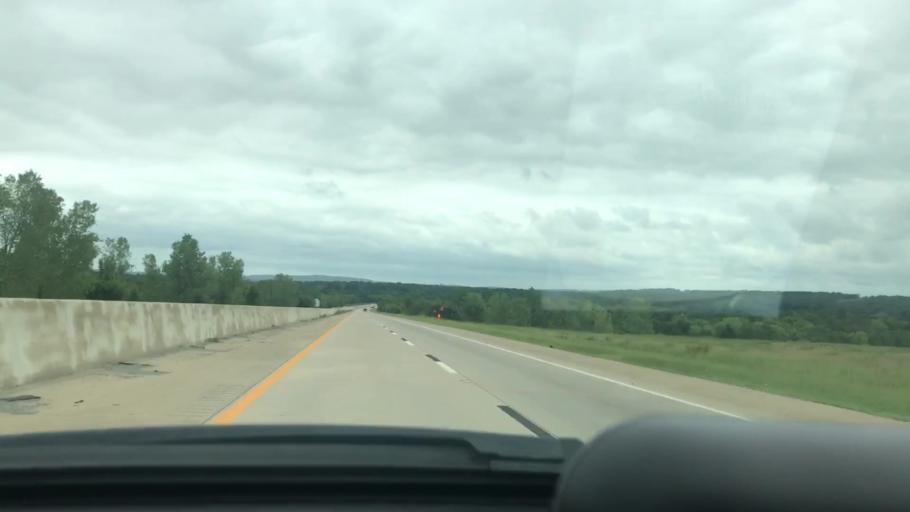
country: US
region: Oklahoma
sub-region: McIntosh County
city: Eufaula
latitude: 35.1846
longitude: -95.6418
